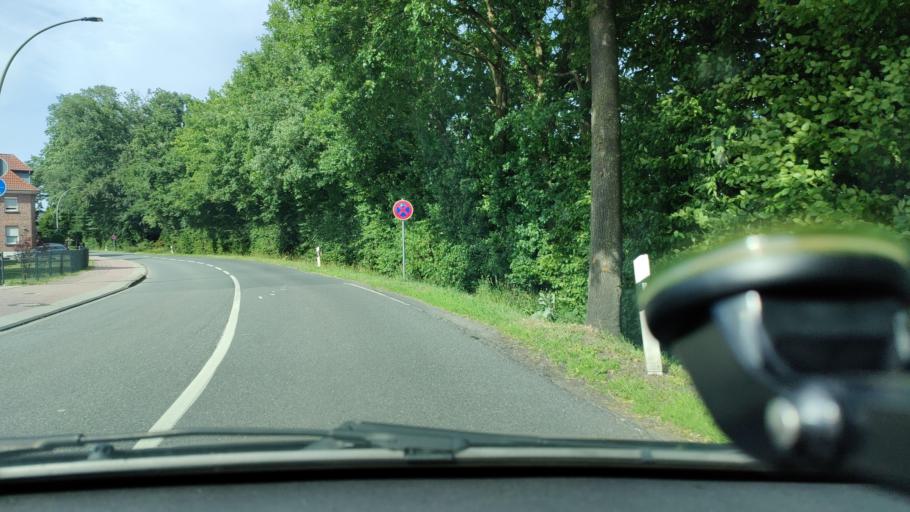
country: DE
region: North Rhine-Westphalia
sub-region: Regierungsbezirk Munster
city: Legden
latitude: 52.0036
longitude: 7.1300
